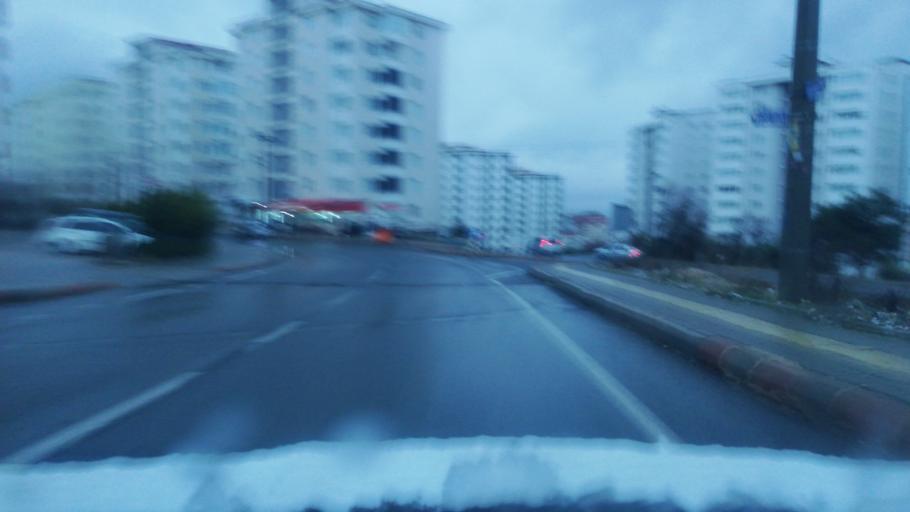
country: TR
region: Kahramanmaras
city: Kahramanmaras
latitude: 37.5984
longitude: 36.8885
